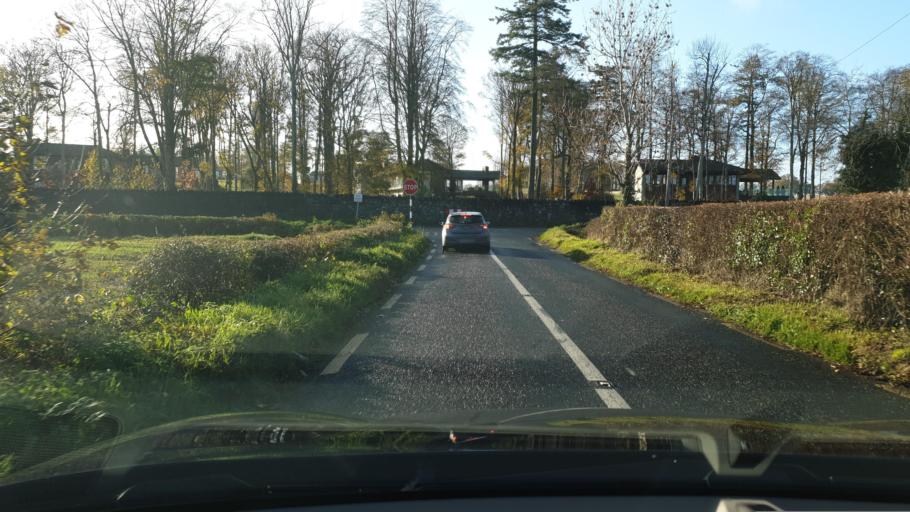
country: IE
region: Leinster
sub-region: Kildare
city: Leixlip
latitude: 53.3890
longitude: -6.5398
